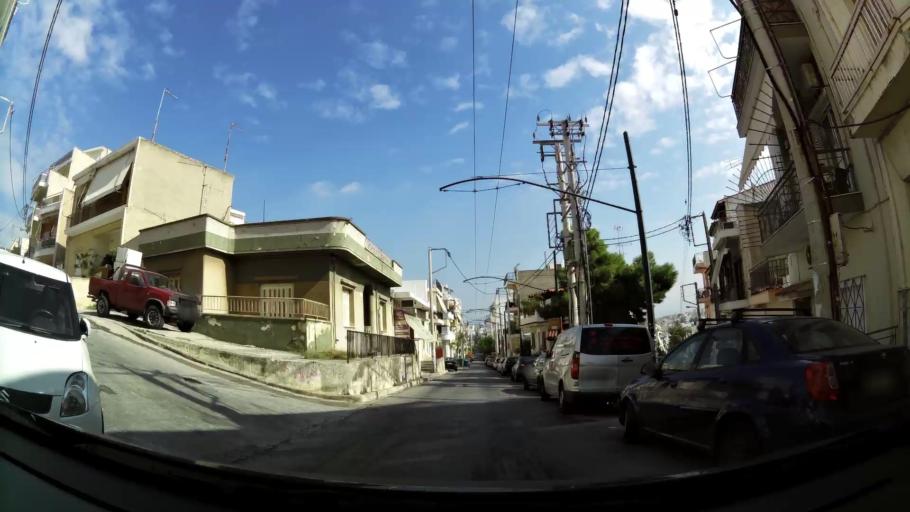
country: GR
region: Attica
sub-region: Nomos Piraios
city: Keratsini
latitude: 37.9613
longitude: 23.6157
